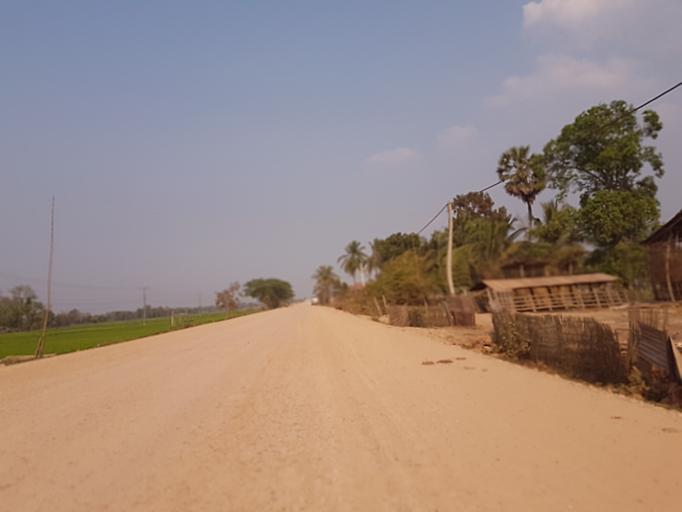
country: TH
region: Nong Khai
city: Phon Phisai
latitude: 17.9877
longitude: 102.8991
